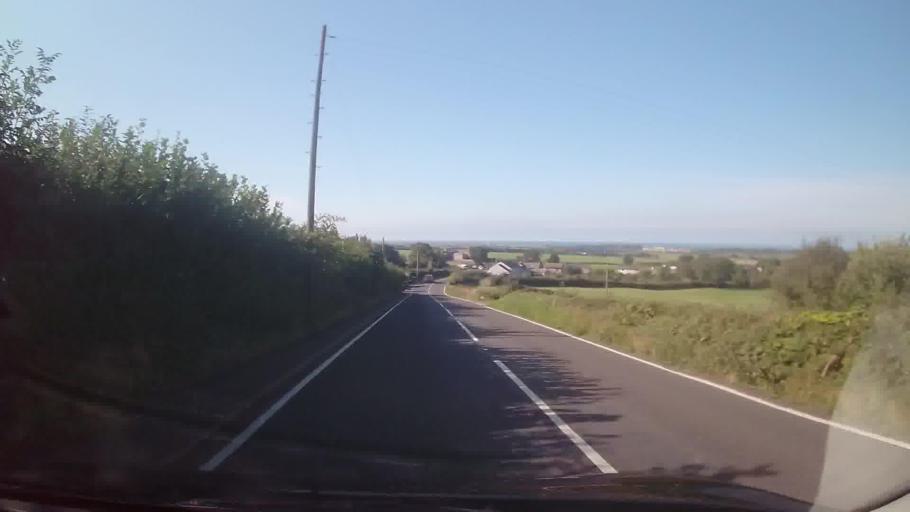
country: GB
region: England
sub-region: Cumbria
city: Seascale
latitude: 54.3296
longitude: -3.3739
